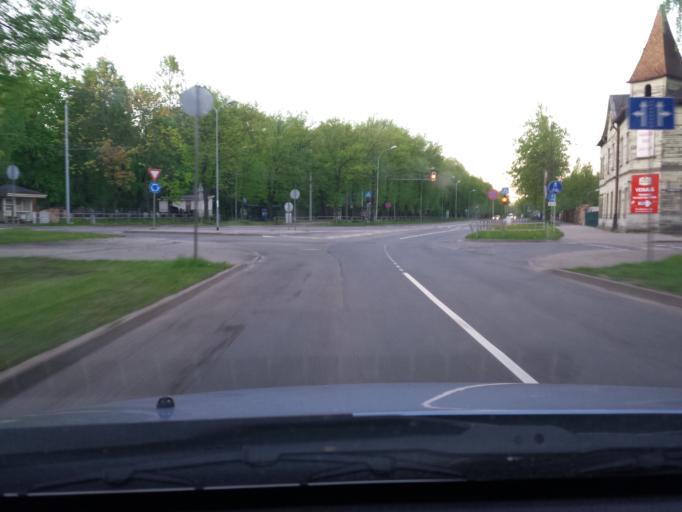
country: LV
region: Riga
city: Riga
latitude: 56.9820
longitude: 24.1500
